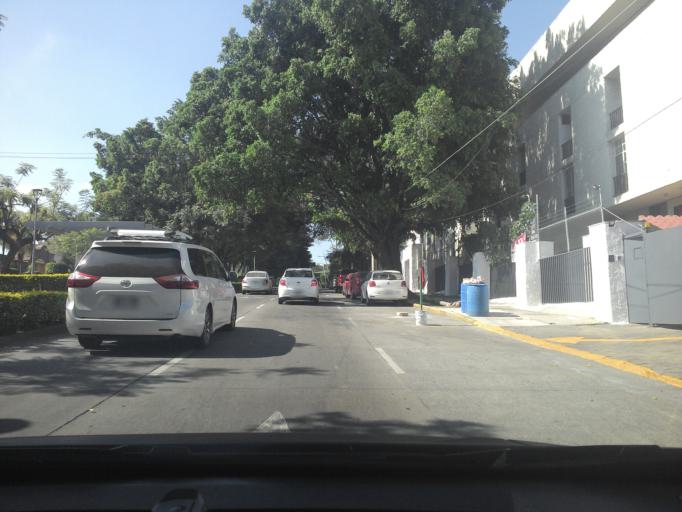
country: MX
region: Jalisco
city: Zapopan2
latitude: 20.6963
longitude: -103.3945
